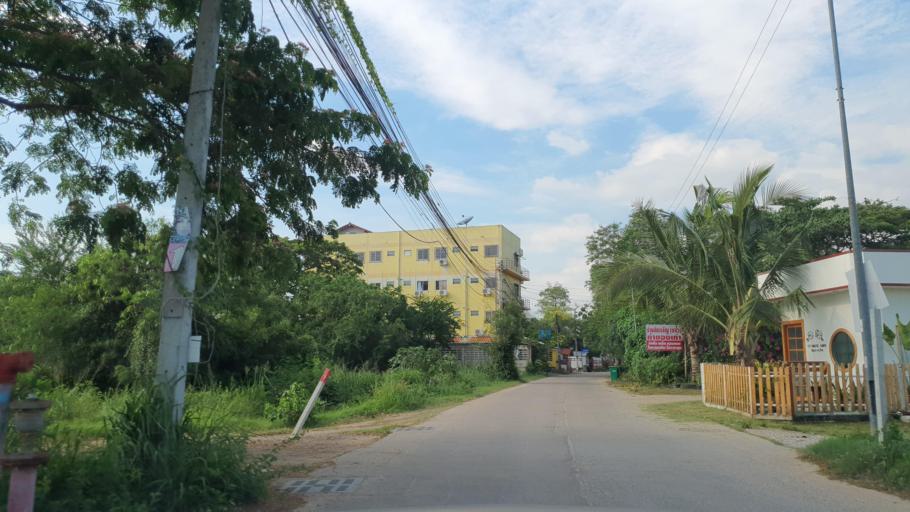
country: TH
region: Chon Buri
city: Phatthaya
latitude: 12.8840
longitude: 100.8895
